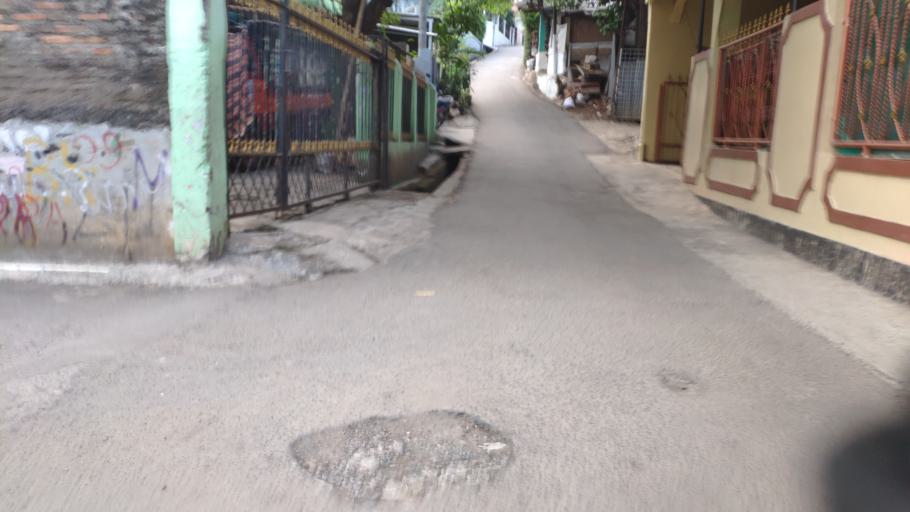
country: ID
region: Jakarta Raya
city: Jakarta
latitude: -6.2973
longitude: 106.8174
